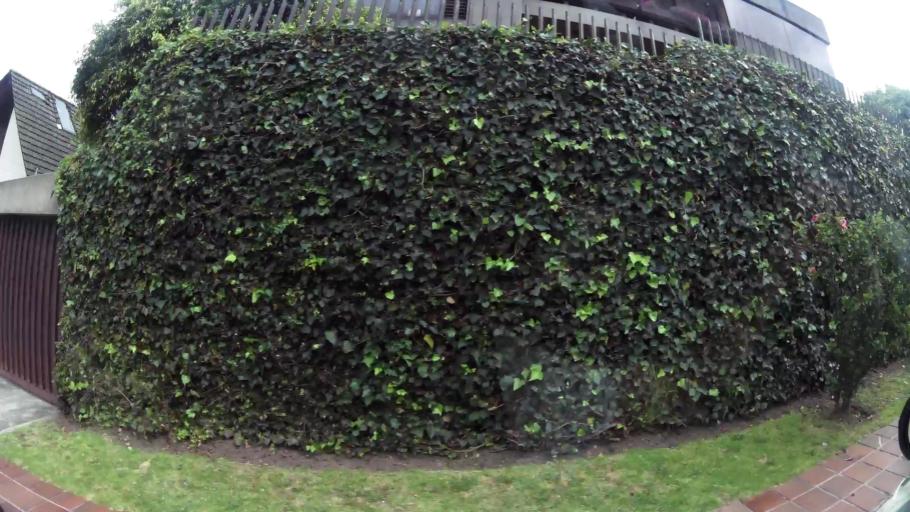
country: EC
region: Pichincha
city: Quito
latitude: -0.1626
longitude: -78.4907
